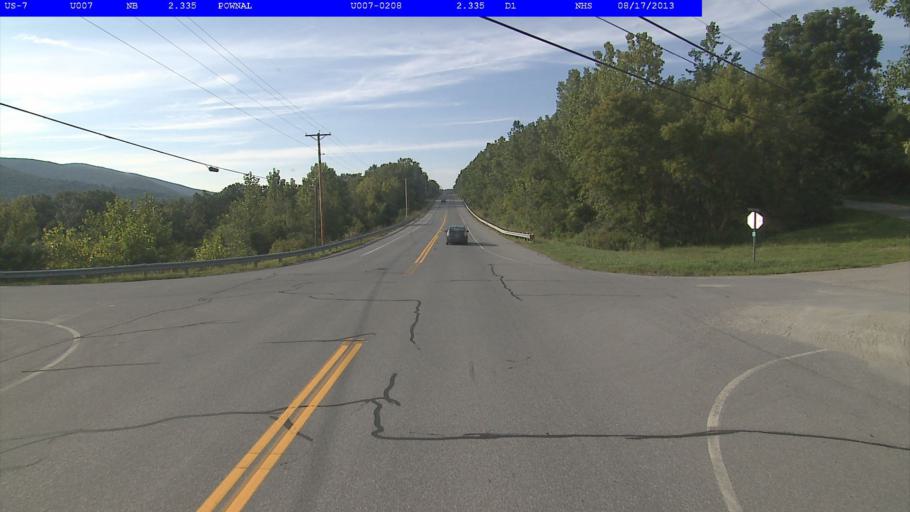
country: US
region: Massachusetts
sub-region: Berkshire County
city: Williamstown
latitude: 42.7697
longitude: -73.2357
